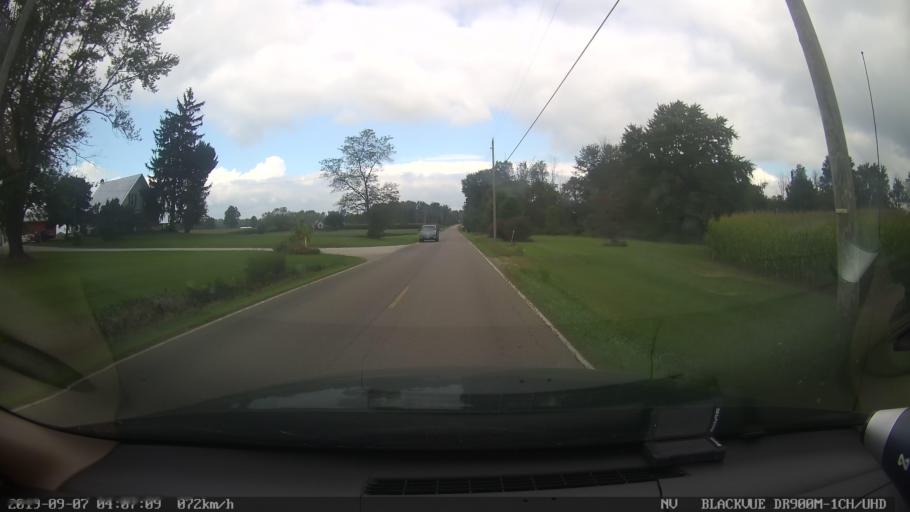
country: US
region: Ohio
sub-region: Licking County
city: Johnstown
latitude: 40.2039
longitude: -82.6109
